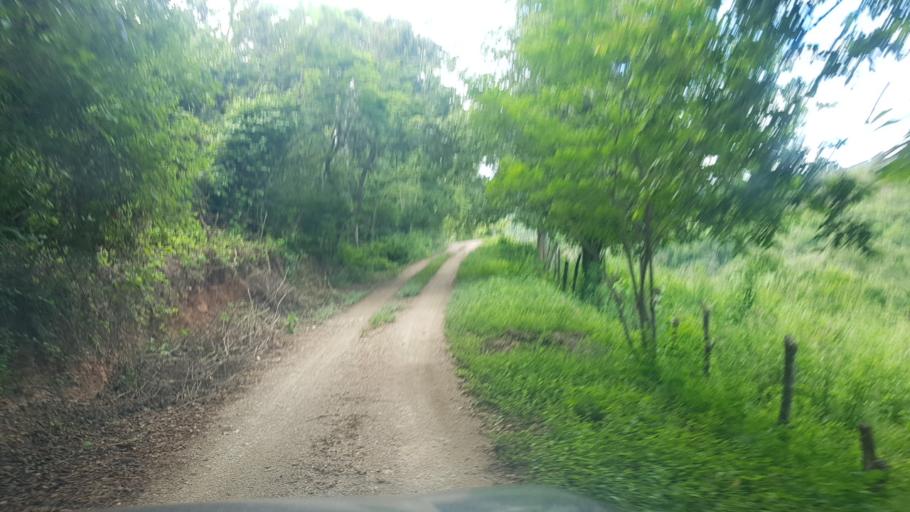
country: NI
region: Nueva Segovia
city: Ocotal
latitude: 13.5942
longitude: -86.4176
